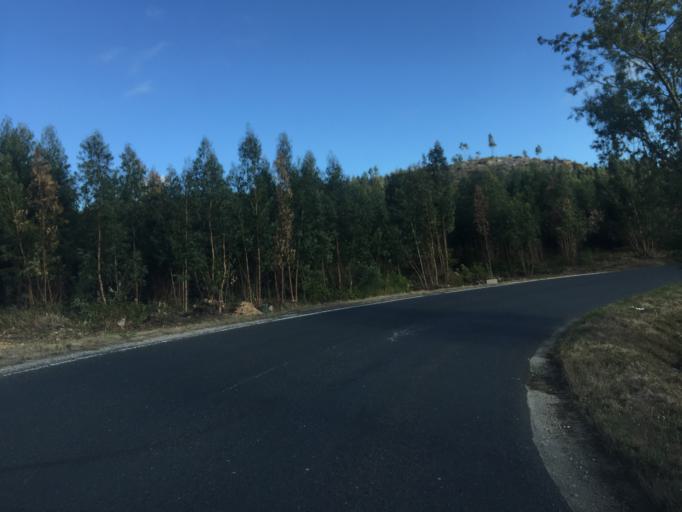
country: PT
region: Lisbon
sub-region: Torres Vedras
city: Torres Vedras
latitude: 39.1286
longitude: -9.2615
